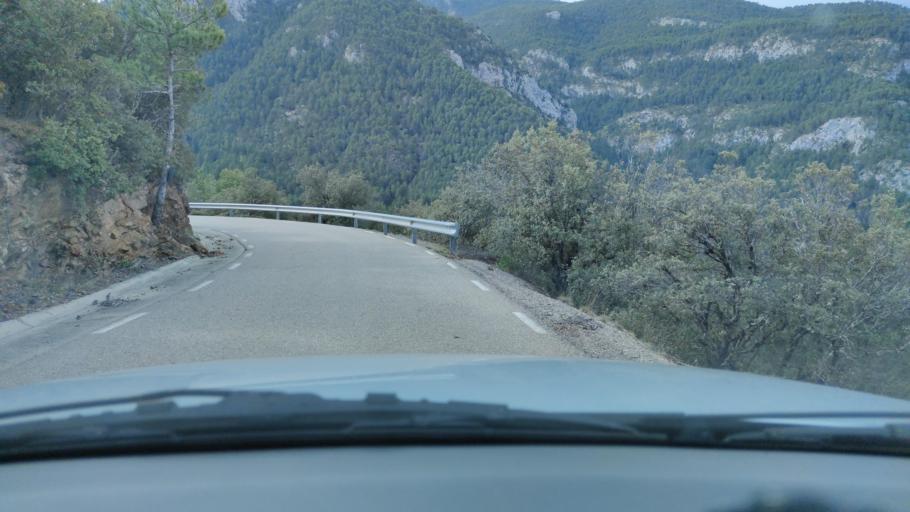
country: ES
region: Catalonia
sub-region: Provincia de Lleida
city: la Seu d'Urgell
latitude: 42.2413
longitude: 1.4282
